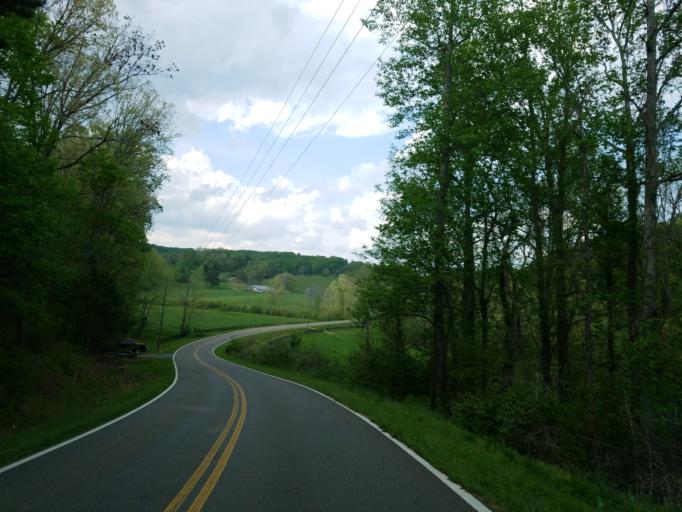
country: US
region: Georgia
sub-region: Pickens County
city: Jasper
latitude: 34.4314
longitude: -84.4521
